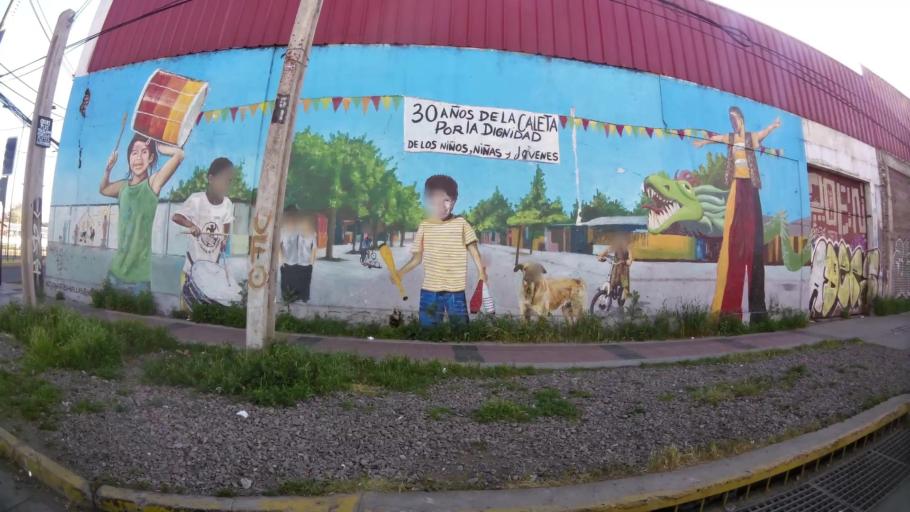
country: CL
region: Santiago Metropolitan
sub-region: Provincia de Santiago
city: Santiago
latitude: -33.4881
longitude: -70.6406
